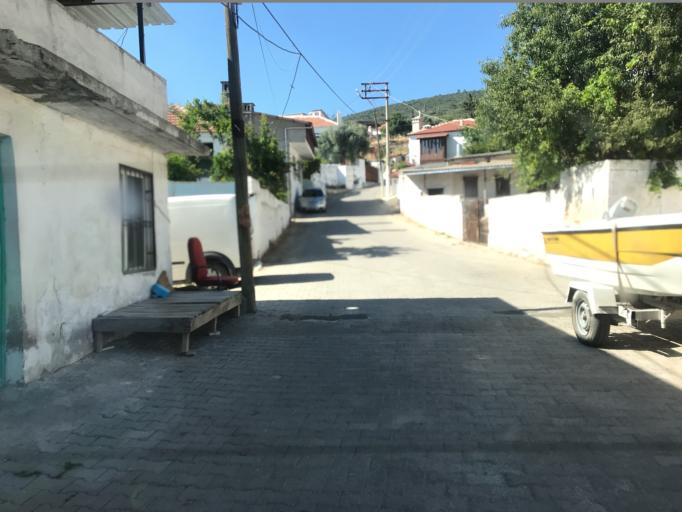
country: TR
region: Mugla
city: Kiulukioi
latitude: 37.3709
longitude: 27.4935
